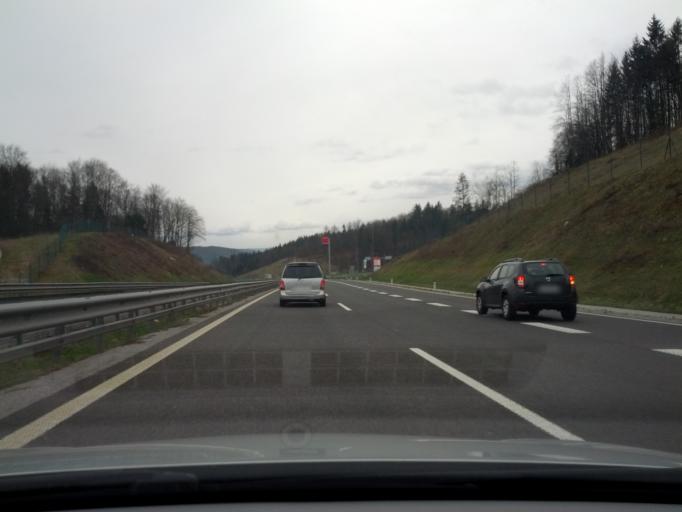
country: SI
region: Trebnje
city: Trebnje
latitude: 45.9008
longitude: 15.0227
